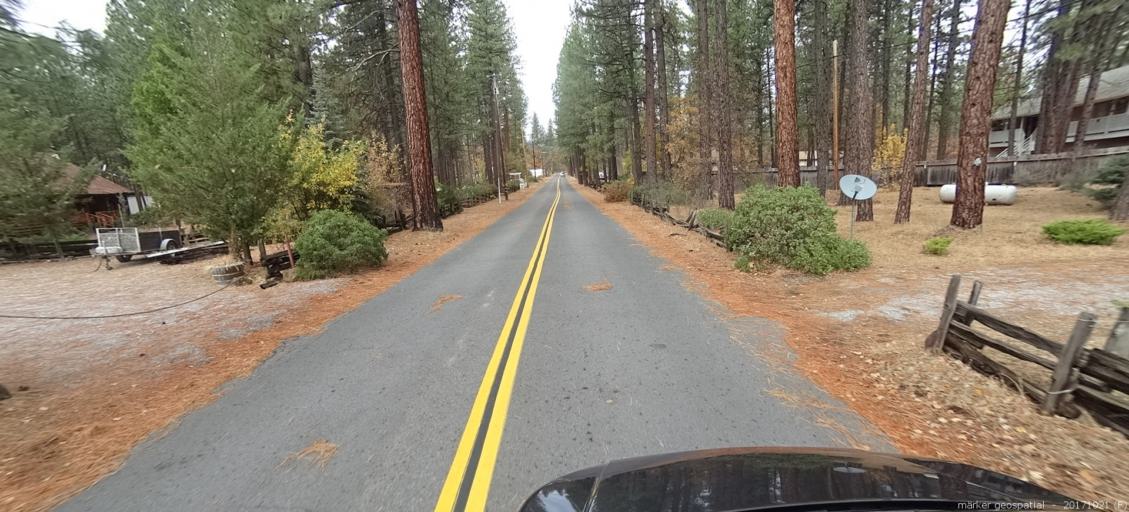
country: US
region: California
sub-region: Shasta County
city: Burney
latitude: 40.9978
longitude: -121.6306
